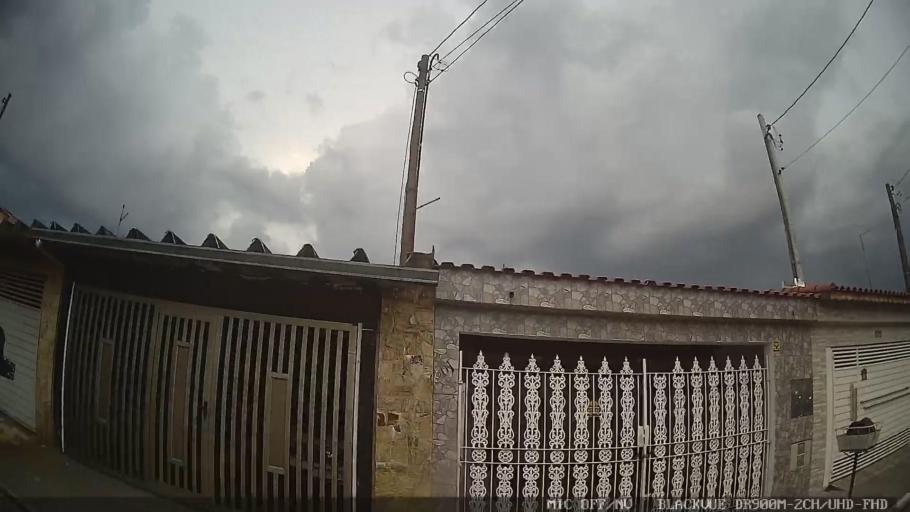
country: BR
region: Sao Paulo
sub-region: Suzano
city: Suzano
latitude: -23.5445
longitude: -46.3033
